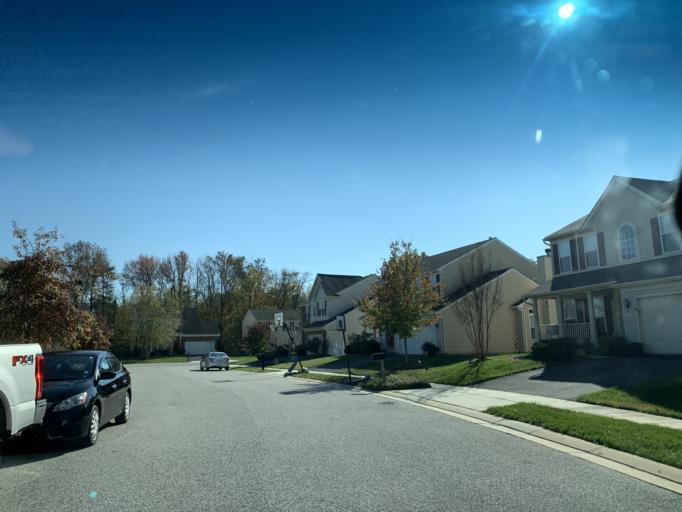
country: US
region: Maryland
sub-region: Baltimore County
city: White Marsh
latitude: 39.4056
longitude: -76.4120
